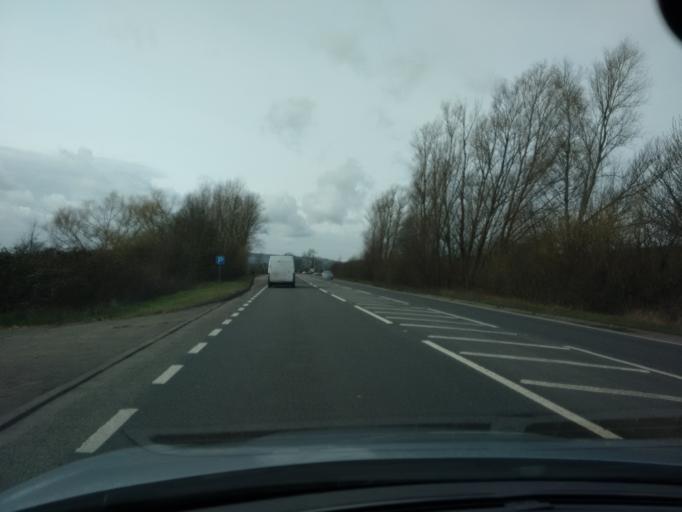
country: GB
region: England
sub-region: Worcestershire
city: Evesham
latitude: 52.0745
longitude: -1.9474
